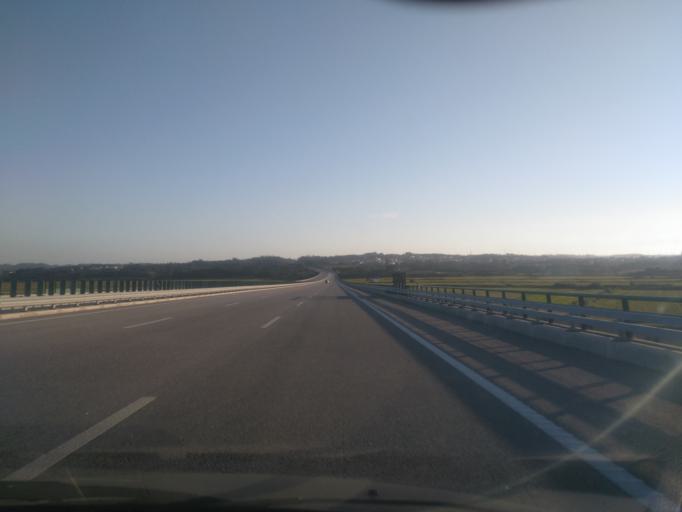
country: PT
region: Coimbra
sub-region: Figueira da Foz
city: Lavos
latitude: 40.1012
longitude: -8.7493
